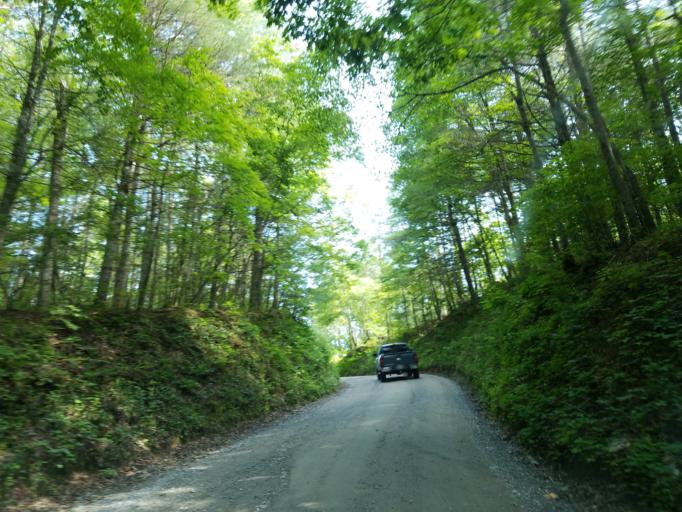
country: US
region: Georgia
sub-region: Fannin County
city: Blue Ridge
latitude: 34.7805
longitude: -84.2334
